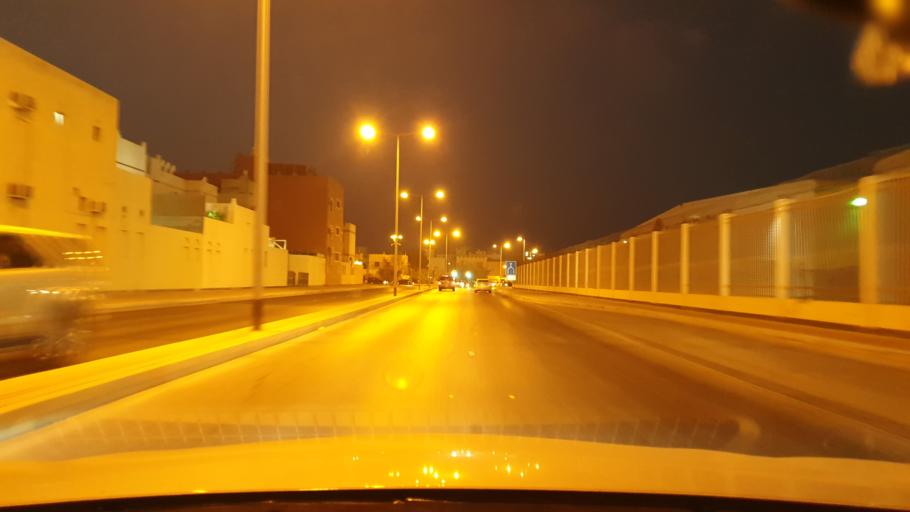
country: BH
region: Muharraq
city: Al Muharraq
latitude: 26.2746
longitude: 50.6131
